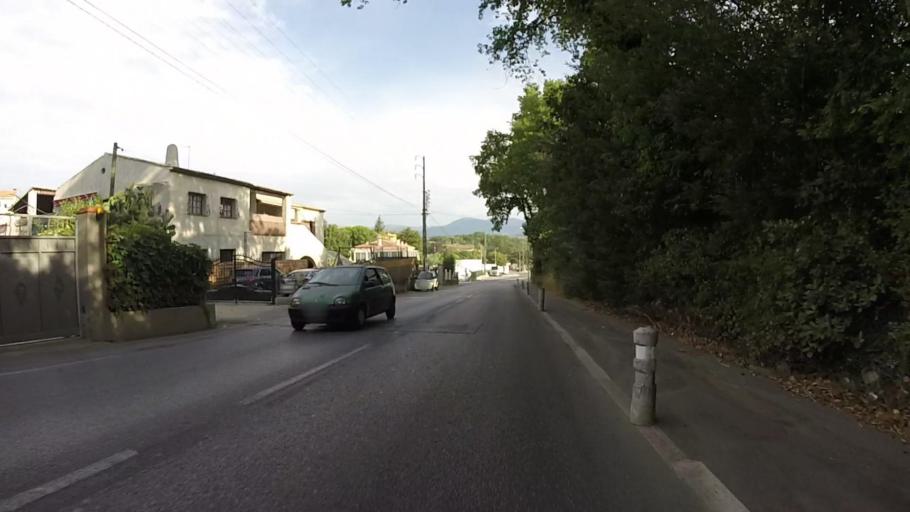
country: FR
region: Provence-Alpes-Cote d'Azur
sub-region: Departement des Alpes-Maritimes
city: Biot
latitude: 43.6064
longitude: 7.1119
